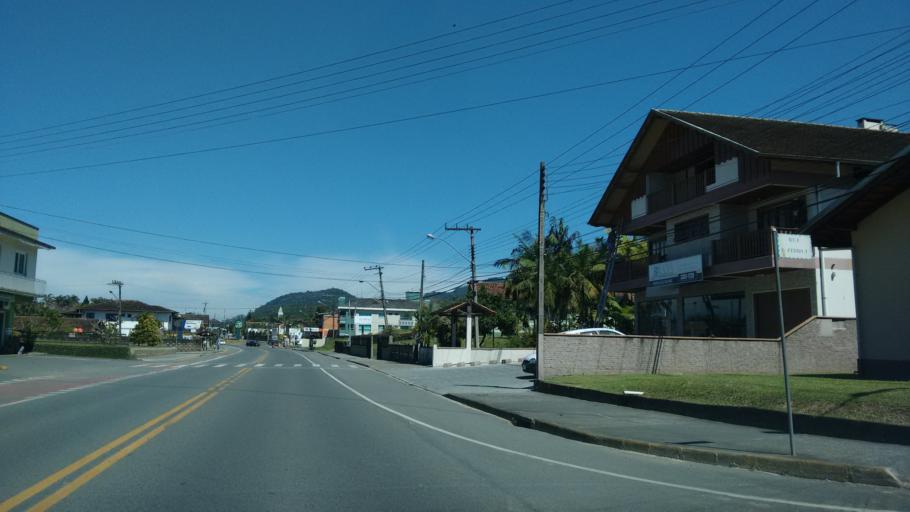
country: BR
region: Santa Catarina
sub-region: Pomerode
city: Pomerode
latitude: -26.7485
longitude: -49.1739
